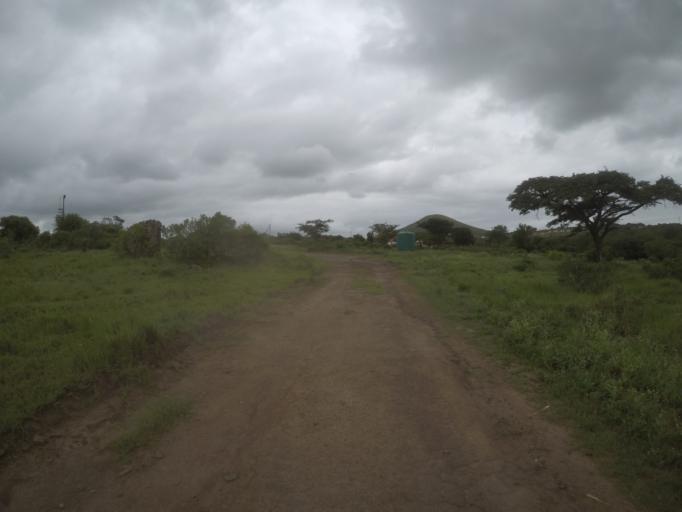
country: ZA
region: KwaZulu-Natal
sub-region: uThungulu District Municipality
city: Empangeni
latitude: -28.5937
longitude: 31.8457
